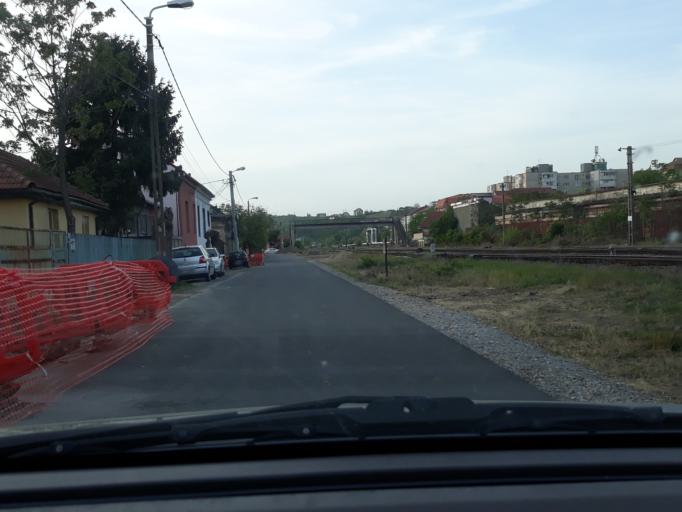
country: RO
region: Bihor
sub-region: Comuna Biharea
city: Oradea
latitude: 47.0456
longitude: 21.9613
